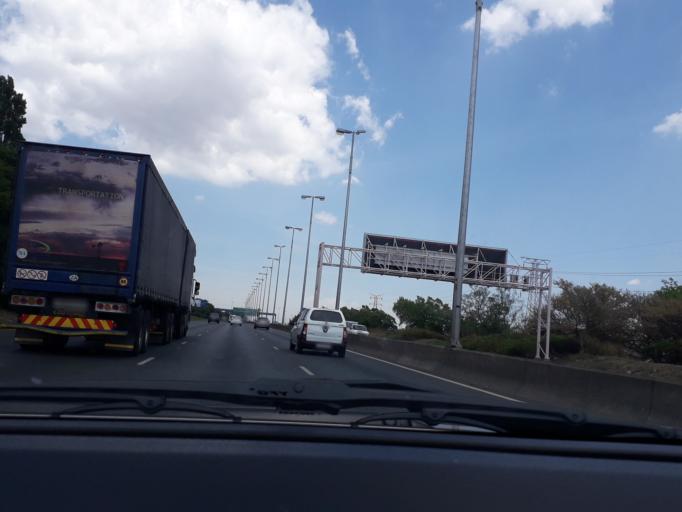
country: ZA
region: Gauteng
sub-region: City of Johannesburg Metropolitan Municipality
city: Johannesburg
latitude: -26.2469
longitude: 28.0032
